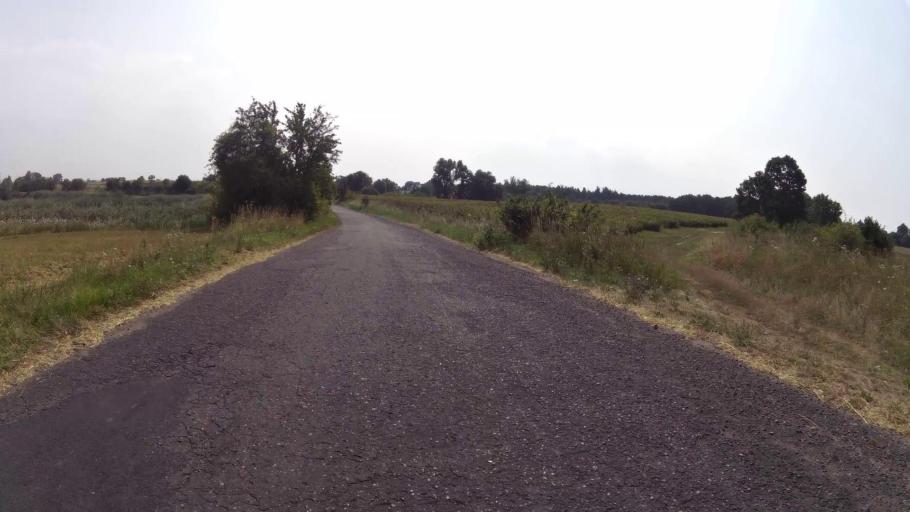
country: PL
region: West Pomeranian Voivodeship
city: Trzcinsko Zdroj
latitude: 52.9338
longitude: 14.5597
